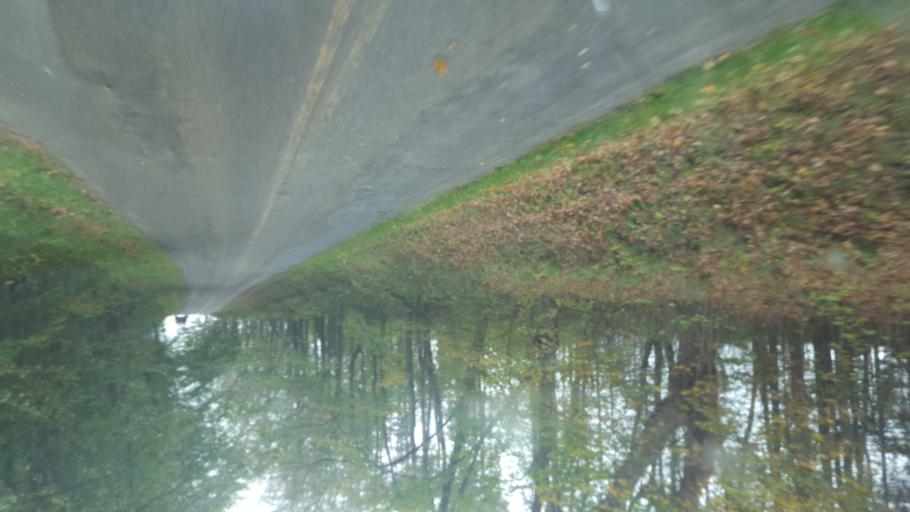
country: US
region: Ohio
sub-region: Carroll County
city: Carrollton
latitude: 40.5318
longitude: -81.1486
